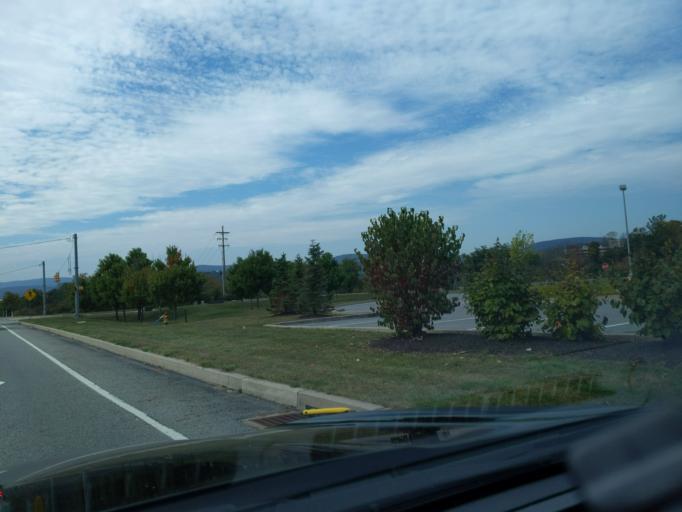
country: US
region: Pennsylvania
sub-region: Blair County
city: Lakemont
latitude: 40.4865
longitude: -78.3877
